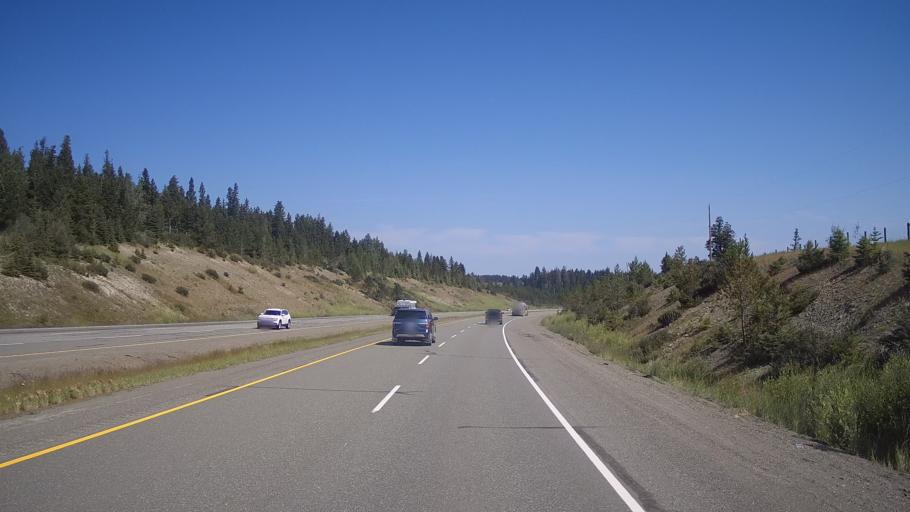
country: CA
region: British Columbia
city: Kamloops
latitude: 50.5289
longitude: -120.4799
